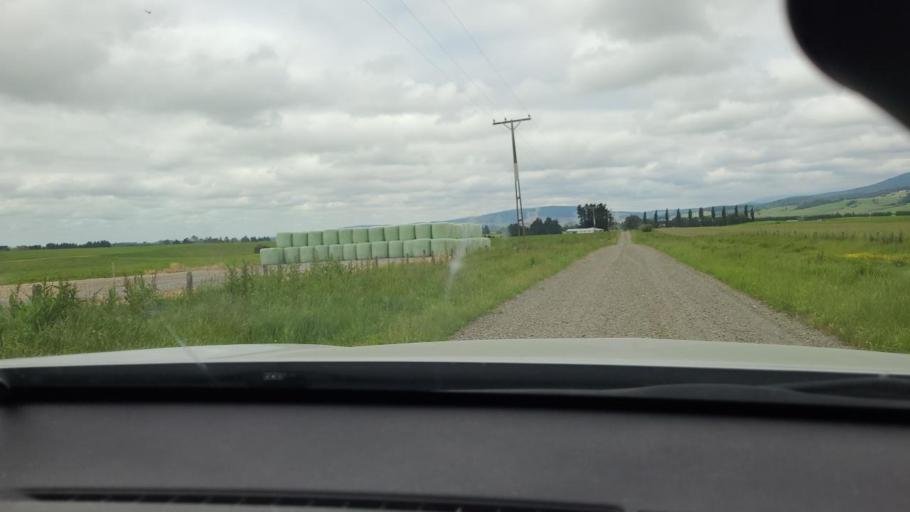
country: NZ
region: Southland
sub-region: Southland District
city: Riverton
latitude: -46.0614
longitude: 167.9471
